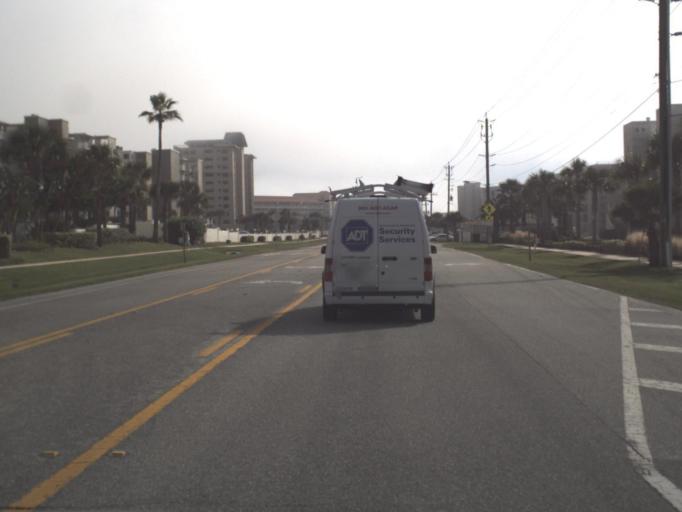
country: US
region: Florida
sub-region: Volusia County
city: Edgewater
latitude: 28.9739
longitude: -80.8562
